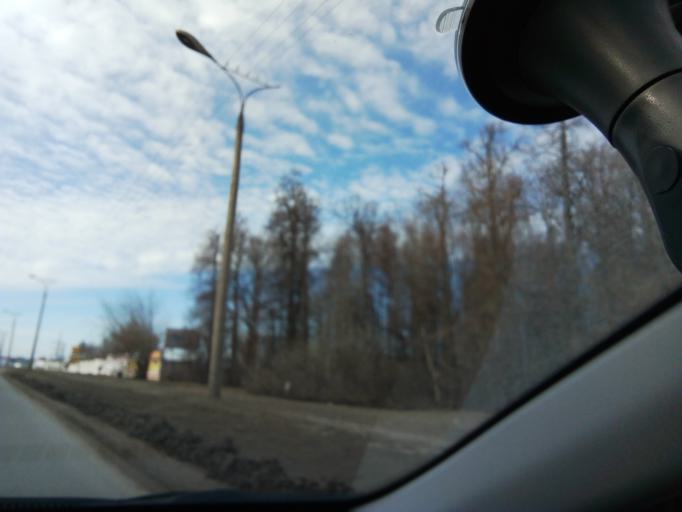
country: RU
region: Chuvashia
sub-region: Cheboksarskiy Rayon
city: Cheboksary
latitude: 56.0982
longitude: 47.2567
